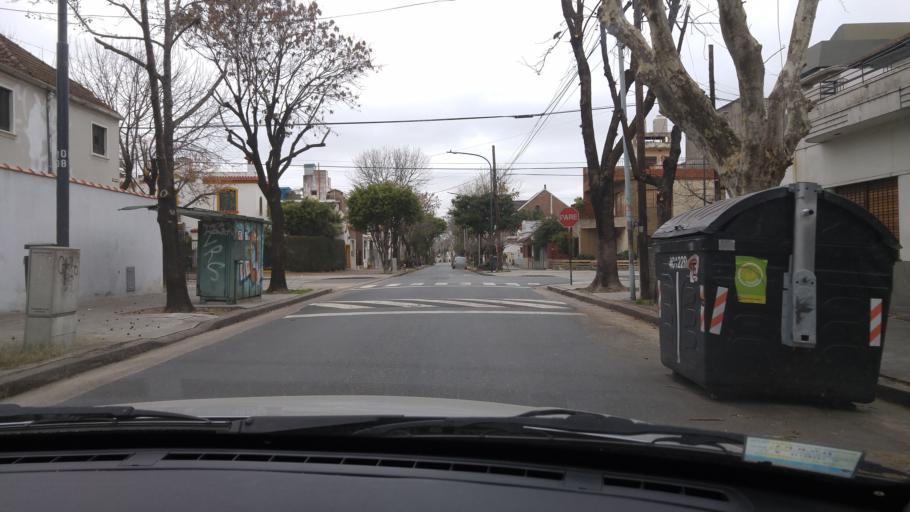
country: AR
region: Buenos Aires
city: Caseros
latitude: -34.6290
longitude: -58.5281
